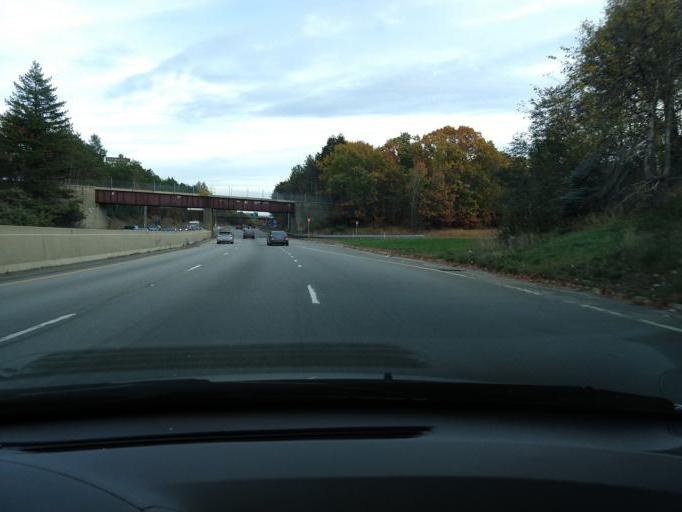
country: US
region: Massachusetts
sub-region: Worcester County
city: Leominster
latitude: 42.5462
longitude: -71.7611
